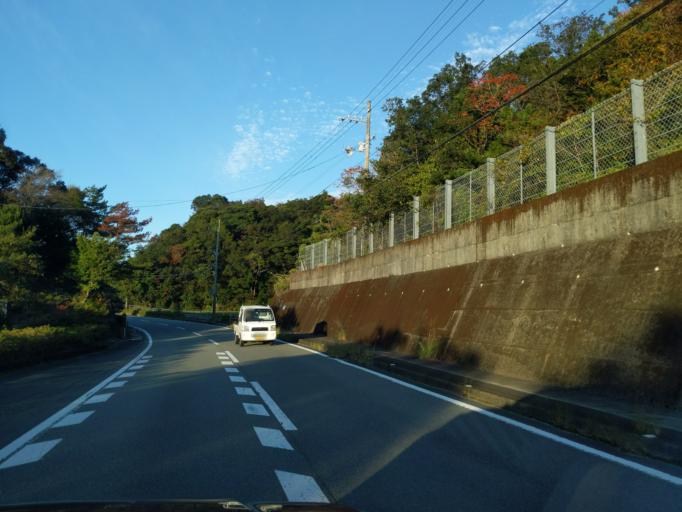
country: JP
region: Kochi
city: Muroto-misakicho
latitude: 33.5854
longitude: 134.3346
